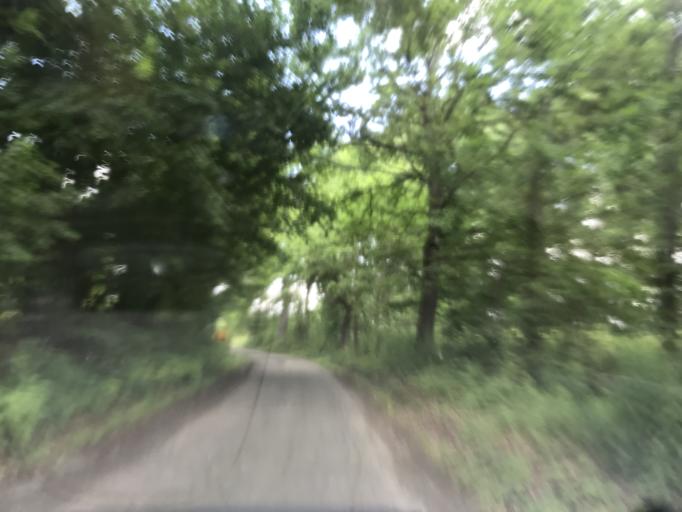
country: PL
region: West Pomeranian Voivodeship
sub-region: Powiat stargardzki
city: Insko
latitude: 53.4932
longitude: 15.4952
